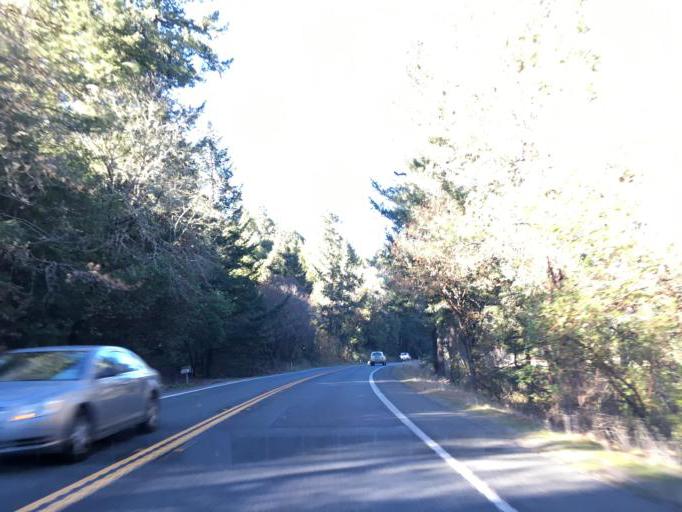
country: US
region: California
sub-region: Mendocino County
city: Brooktrails
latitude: 39.4891
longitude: -123.3625
